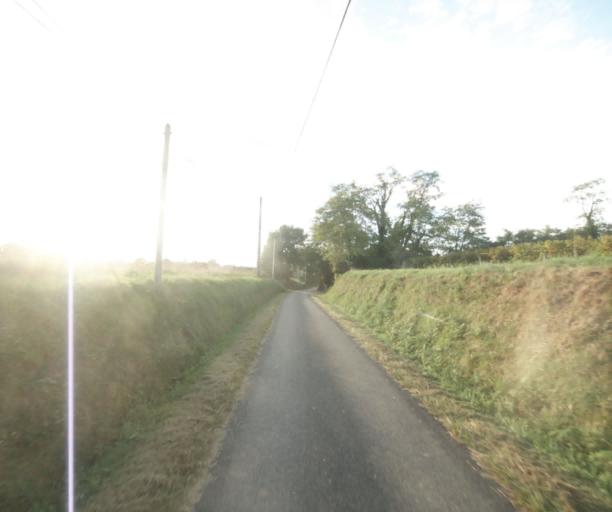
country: FR
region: Midi-Pyrenees
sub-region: Departement du Gers
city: Le Houga
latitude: 43.8421
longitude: -0.1134
